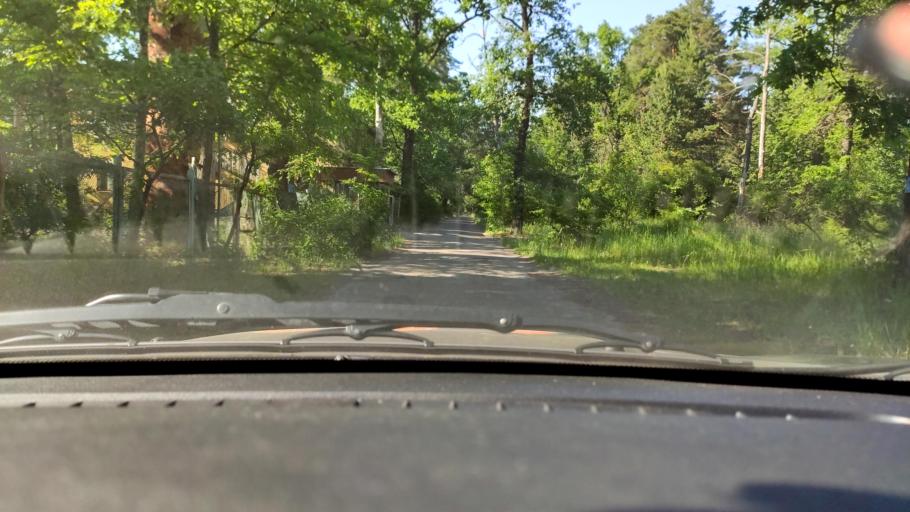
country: RU
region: Voronezj
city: Somovo
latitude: 51.7531
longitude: 39.3745
